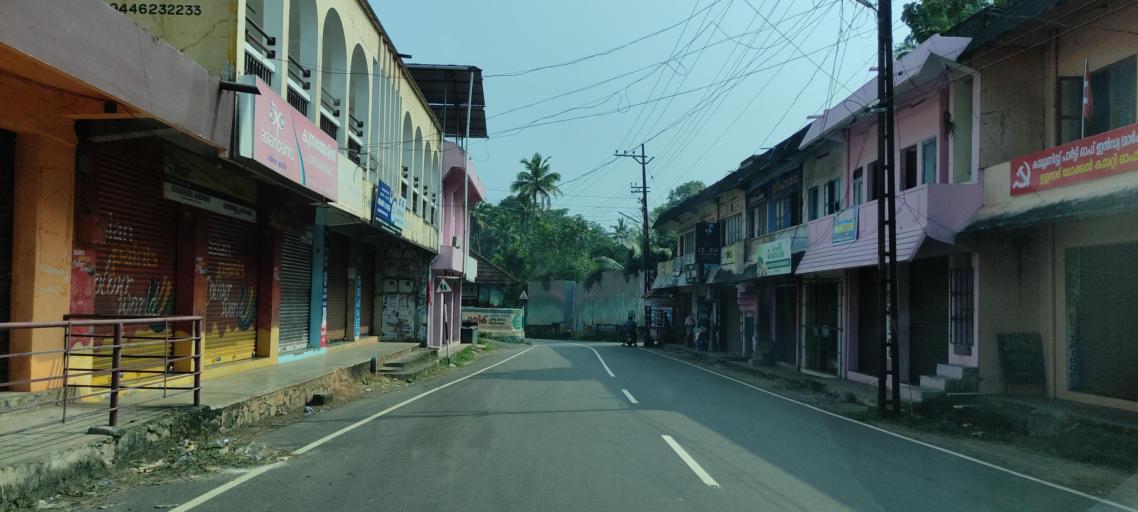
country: IN
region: Kerala
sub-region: Pattanamtitta
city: Adur
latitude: 9.2361
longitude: 76.6965
